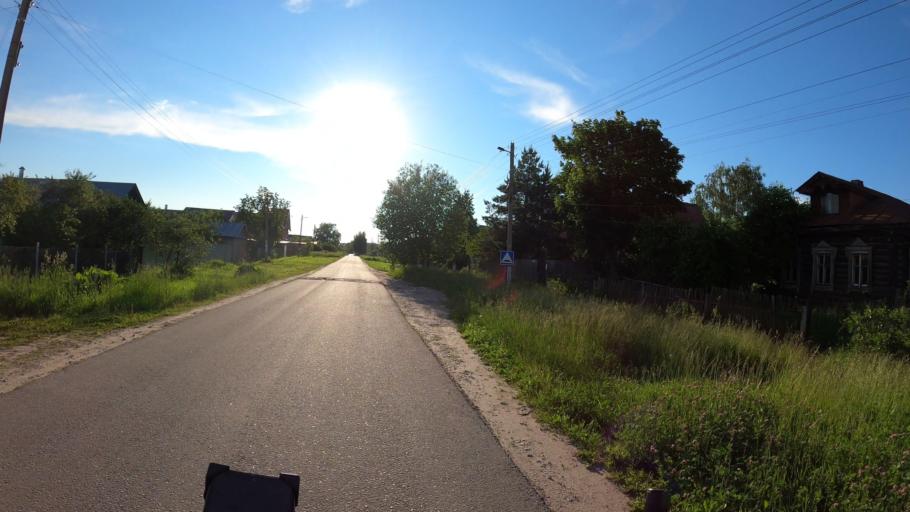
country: RU
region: Moskovskaya
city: Ashitkovo
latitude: 55.4549
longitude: 38.5879
